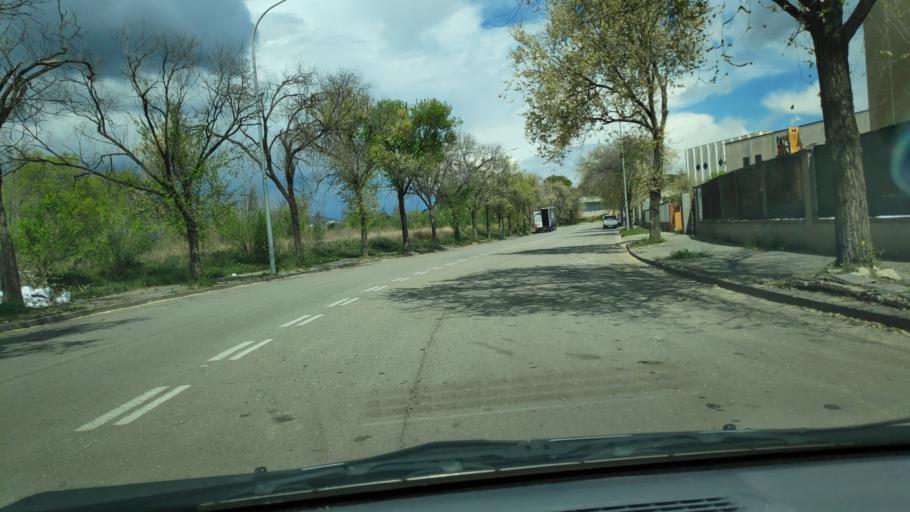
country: ES
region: Catalonia
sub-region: Provincia de Barcelona
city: Barbera del Valles
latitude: 41.5359
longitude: 2.1287
